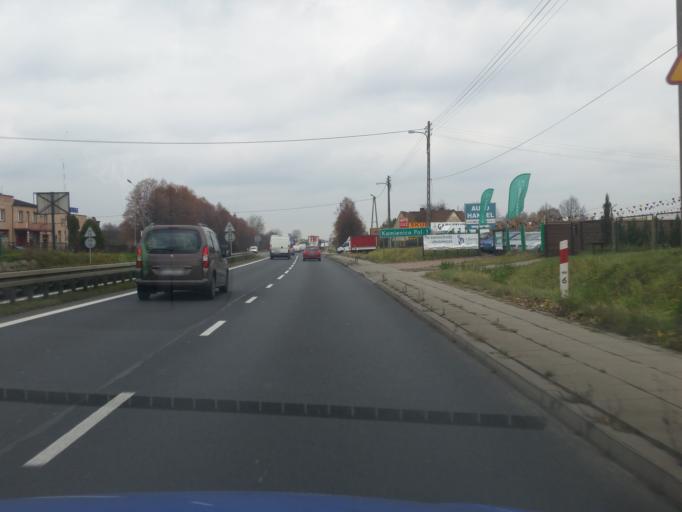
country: PL
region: Silesian Voivodeship
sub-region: Powiat czestochowski
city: Kamienica Polska
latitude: 50.6913
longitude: 19.1356
